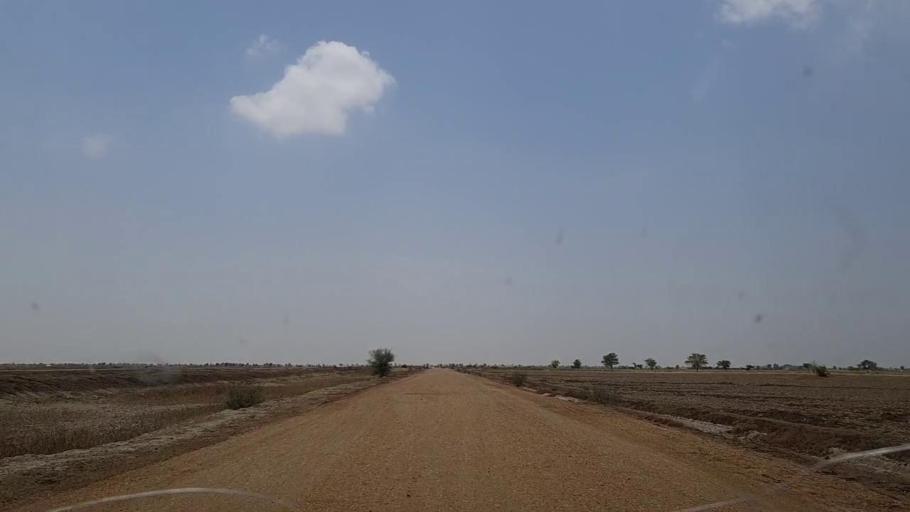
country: PK
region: Sindh
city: Phulji
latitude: 26.7885
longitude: 67.6444
